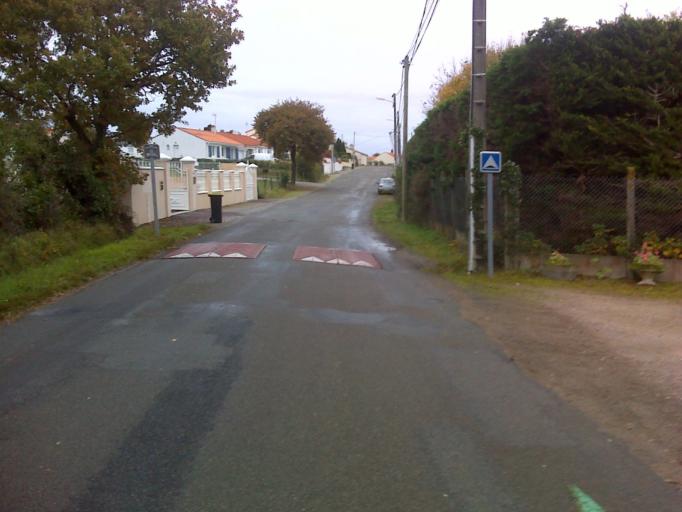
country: FR
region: Pays de la Loire
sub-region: Departement de la Loire-Atlantique
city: La Bernerie-en-Retz
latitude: 47.0840
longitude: -2.0285
